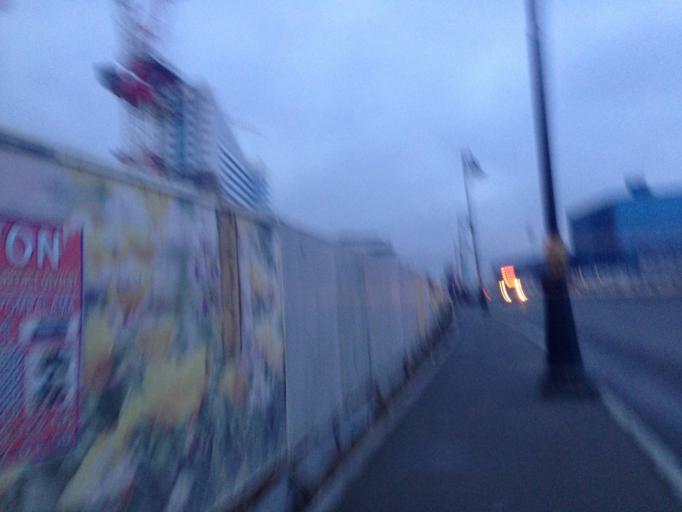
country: AZ
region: Baki
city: Baku
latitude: 40.4134
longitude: 49.8972
